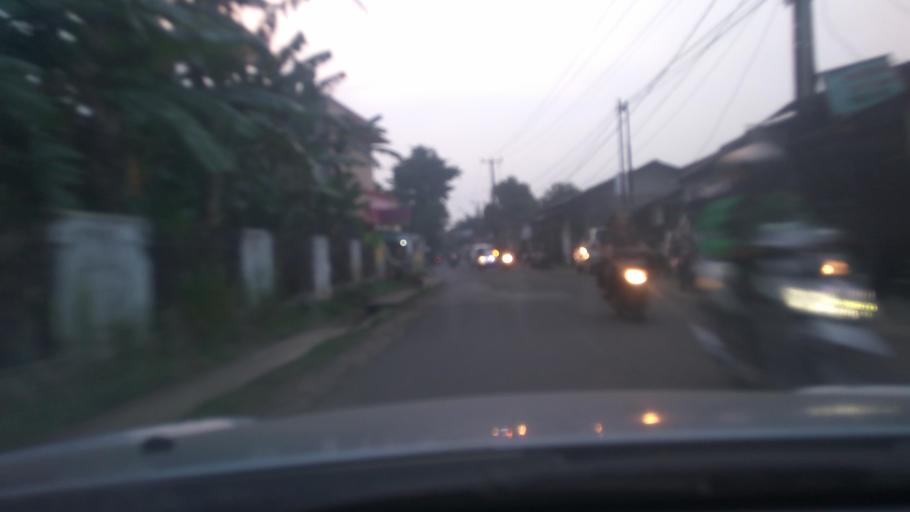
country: ID
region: West Java
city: Pamulang
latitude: -6.3689
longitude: 106.7443
